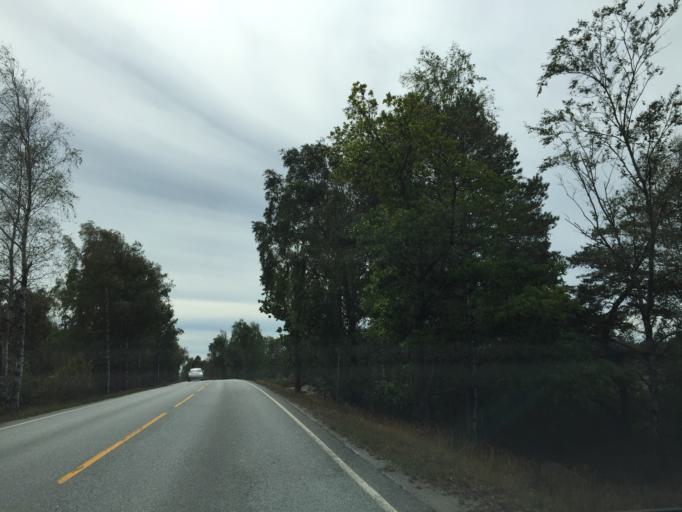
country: NO
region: Ostfold
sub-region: Fredrikstad
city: Fredrikstad
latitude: 59.0907
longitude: 10.9266
